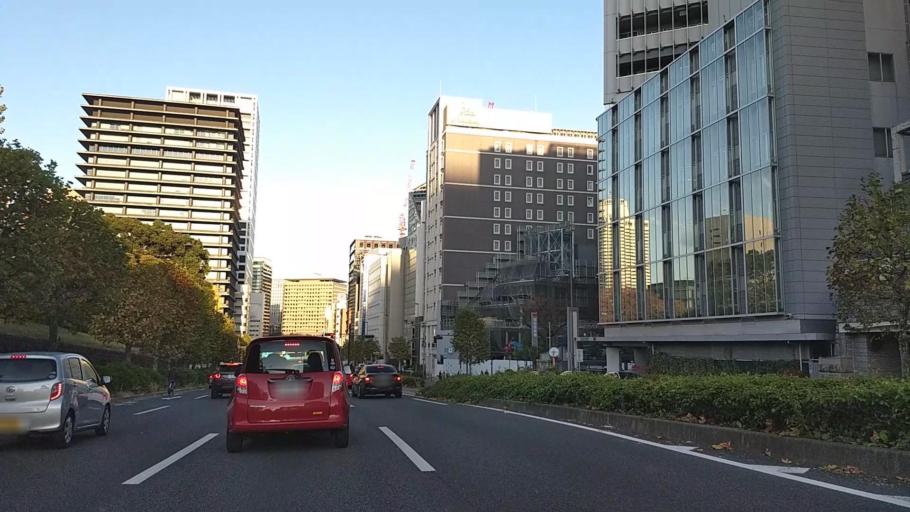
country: JP
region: Tokyo
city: Tokyo
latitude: 35.6751
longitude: 139.7315
